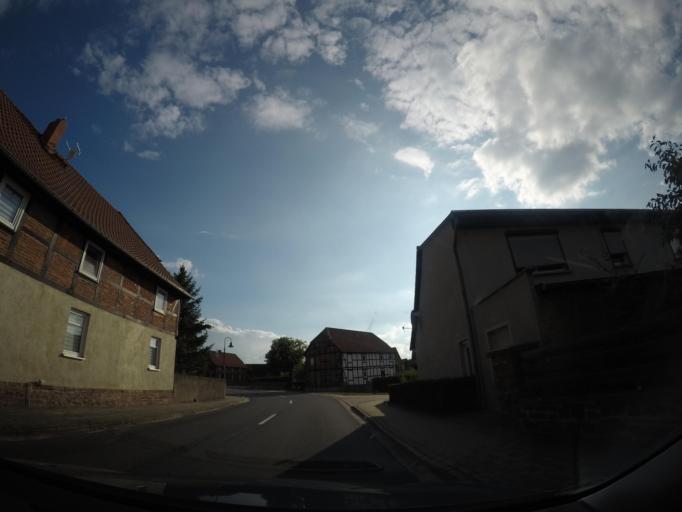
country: DE
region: Saxony-Anhalt
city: Weferlingen
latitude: 52.3676
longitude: 11.0965
